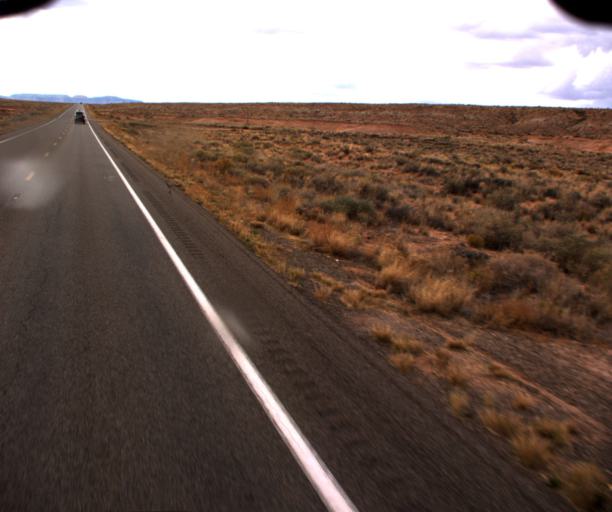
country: US
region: Arizona
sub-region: Navajo County
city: Kayenta
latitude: 36.7463
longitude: -110.0702
